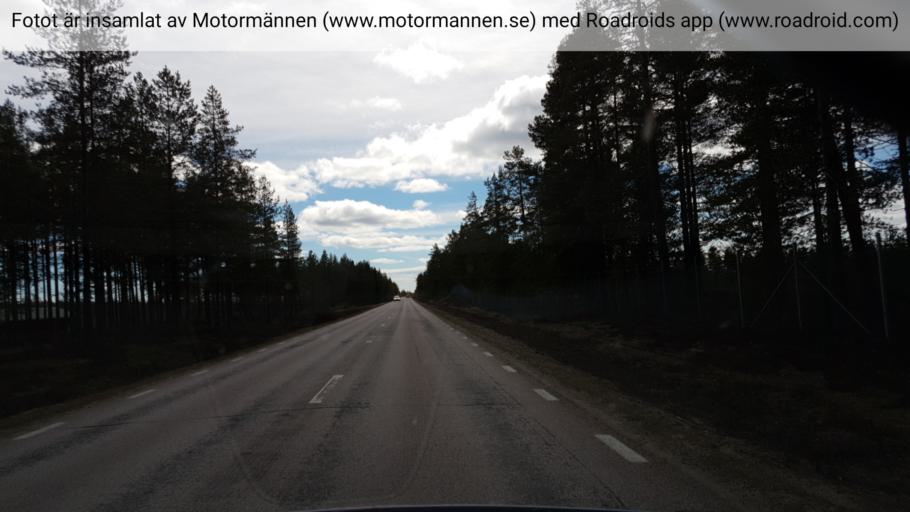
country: SE
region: Vaesternorrland
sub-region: OErnskoeldsviks Kommun
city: Husum
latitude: 63.4568
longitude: 18.9568
